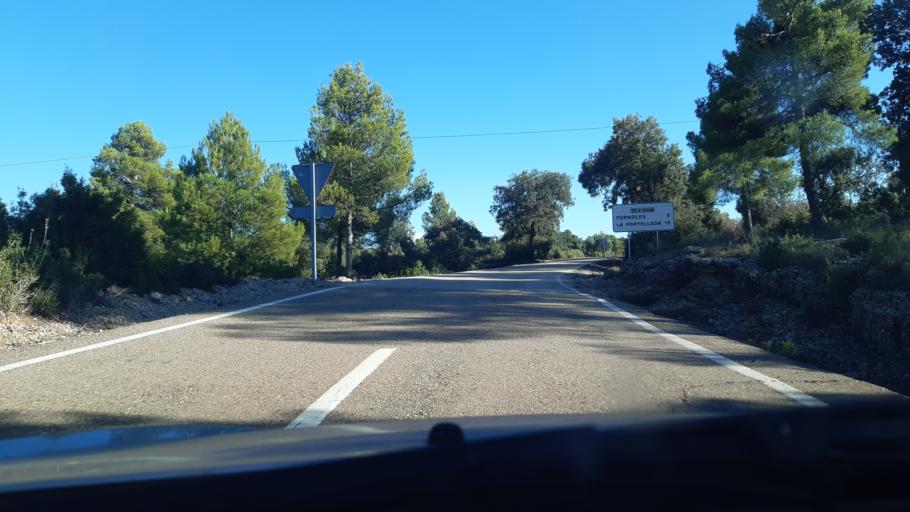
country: ES
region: Aragon
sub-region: Provincia de Teruel
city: Fornoles
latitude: 40.9141
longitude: -0.0200
